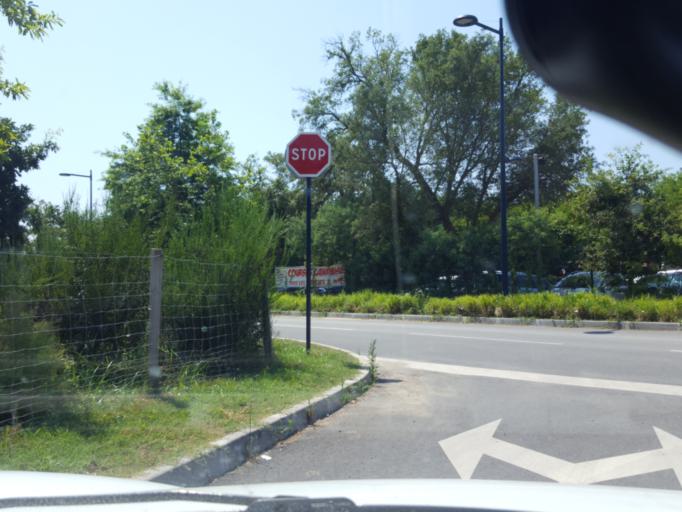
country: FR
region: Aquitaine
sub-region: Departement des Landes
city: Ondres
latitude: 43.5736
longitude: -1.4702
